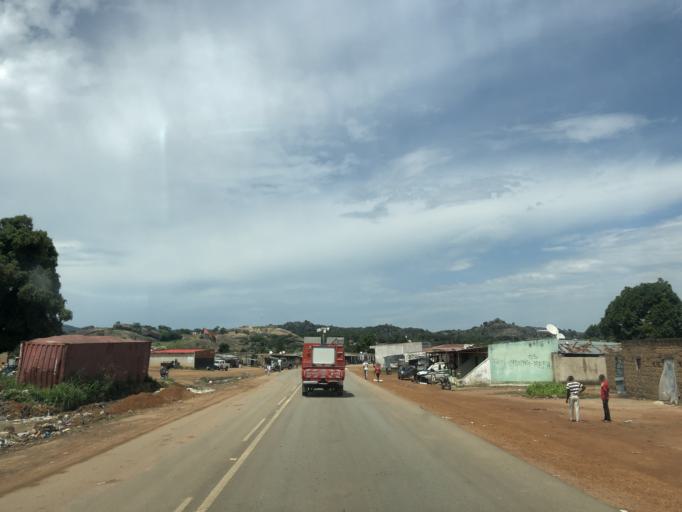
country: AO
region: Cuanza Sul
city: Quibala
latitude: -10.7362
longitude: 14.9897
